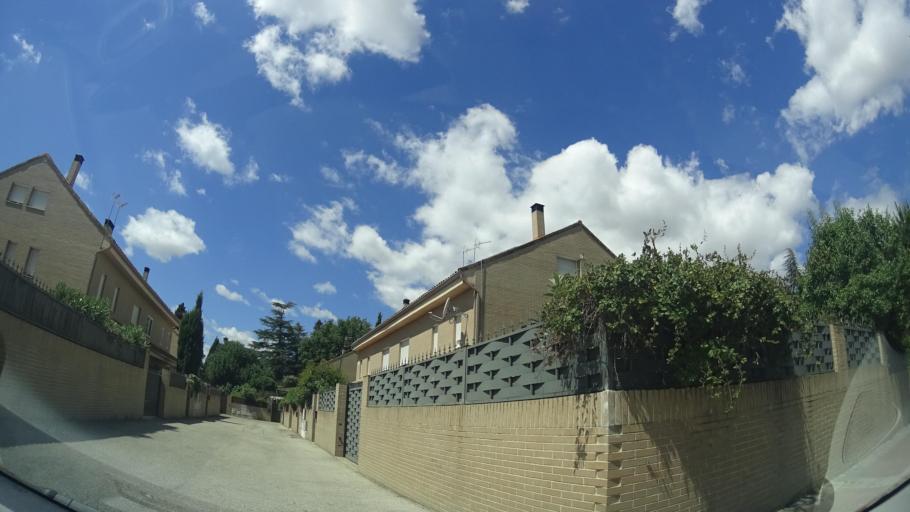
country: ES
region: Madrid
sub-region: Provincia de Madrid
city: Collado-Villalba
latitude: 40.6236
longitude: -3.9935
